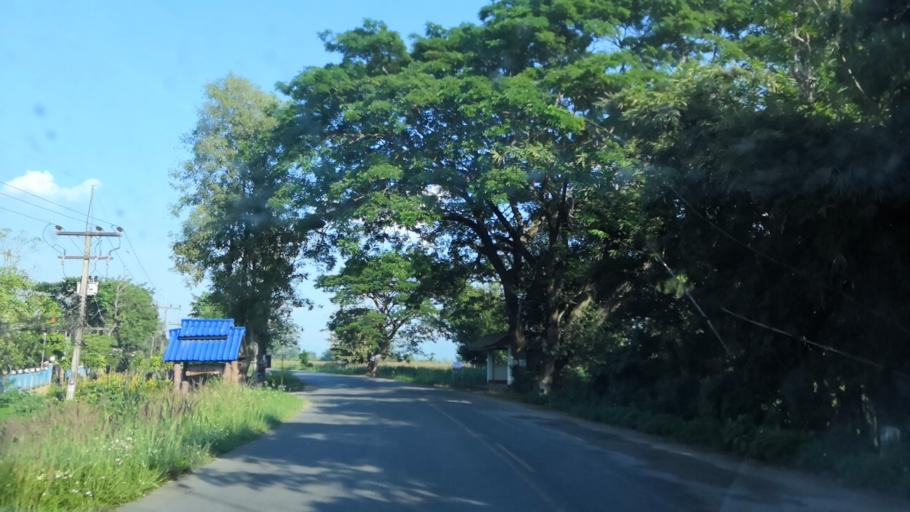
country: TH
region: Chiang Rai
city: Wiang Chai
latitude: 19.9473
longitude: 99.9263
